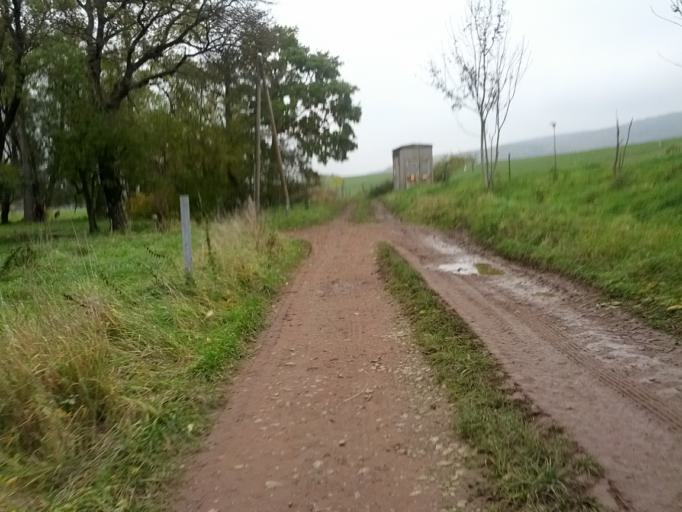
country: DE
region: Thuringia
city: Seebach
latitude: 50.9793
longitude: 10.4338
